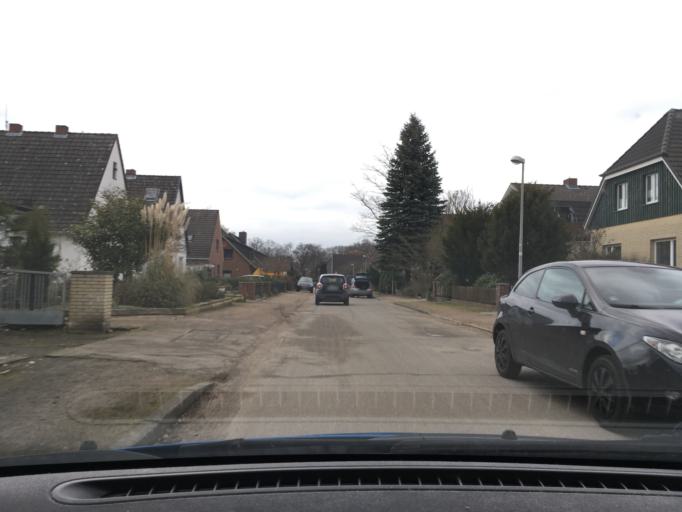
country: DE
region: Schleswig-Holstein
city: Wedel
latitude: 53.5807
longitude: 9.7177
